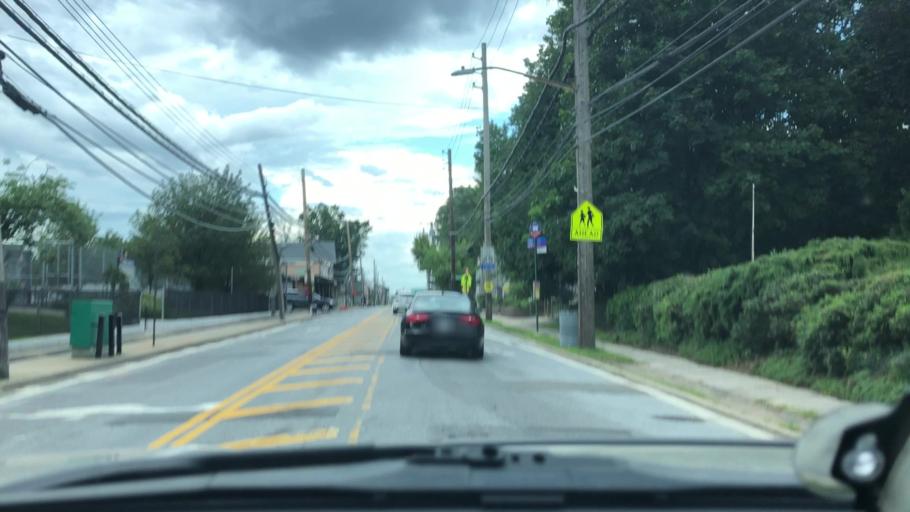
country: US
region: New York
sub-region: Richmond County
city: Bloomfield
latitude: 40.5920
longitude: -74.1902
